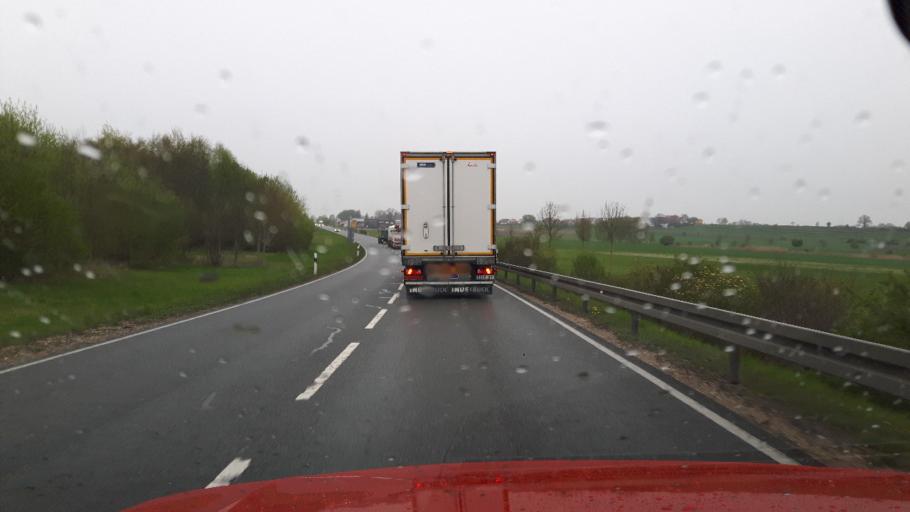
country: DE
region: Bavaria
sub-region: Regierungsbezirk Mittelfranken
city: Muhr am See
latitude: 49.1496
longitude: 10.7320
